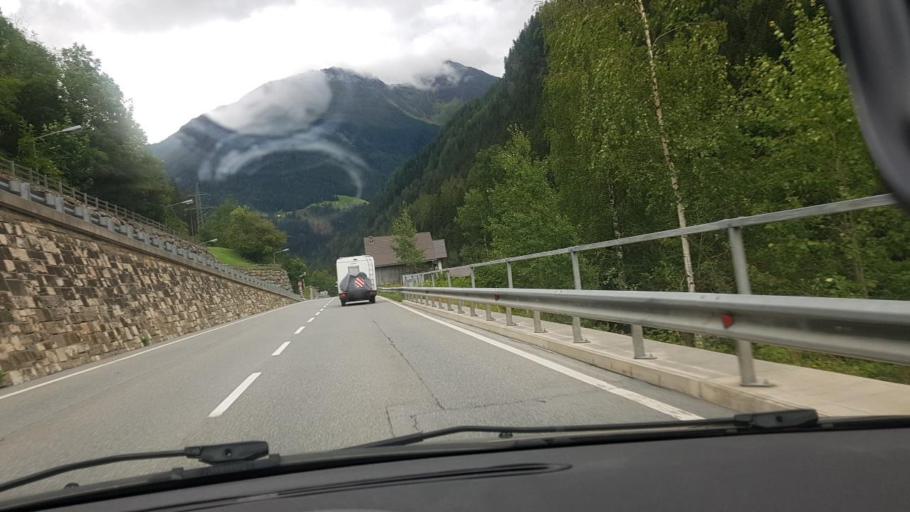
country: AT
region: Tyrol
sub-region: Politischer Bezirk Landeck
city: Strengen
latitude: 47.1240
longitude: 10.4650
